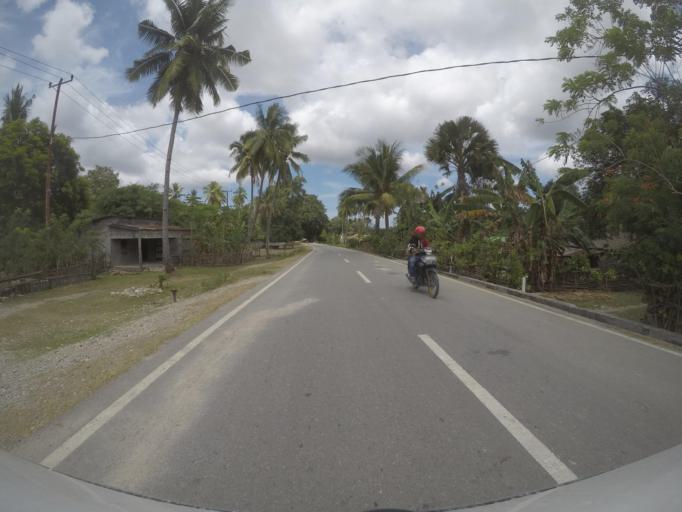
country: TL
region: Viqueque
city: Viqueque
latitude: -8.8805
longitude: 126.3758
